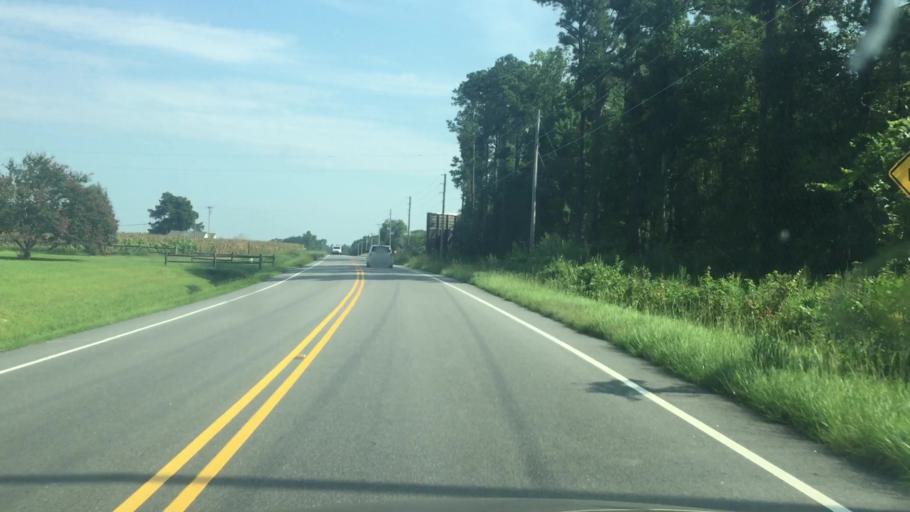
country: US
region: North Carolina
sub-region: Columbus County
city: Tabor City
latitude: 34.2170
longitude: -78.8239
